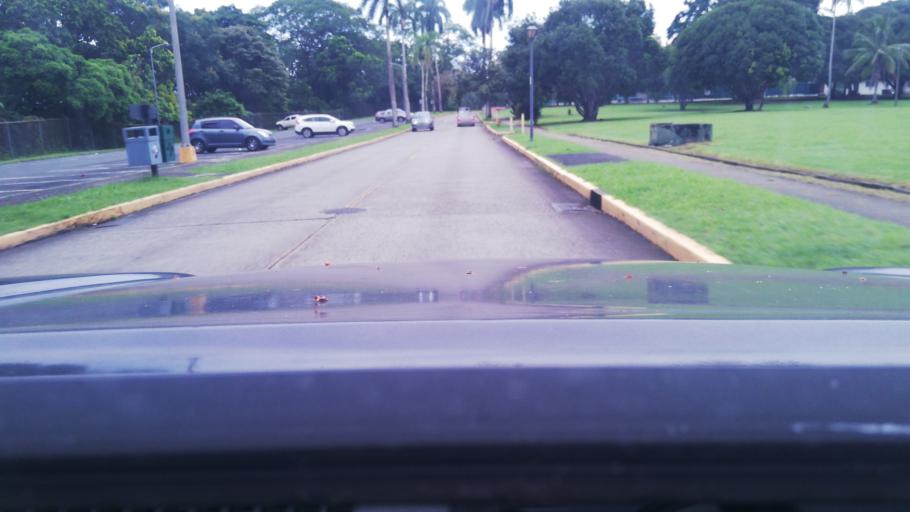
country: PA
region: Panama
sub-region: Distrito de Panama
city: Ancon
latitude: 8.9982
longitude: -79.5778
